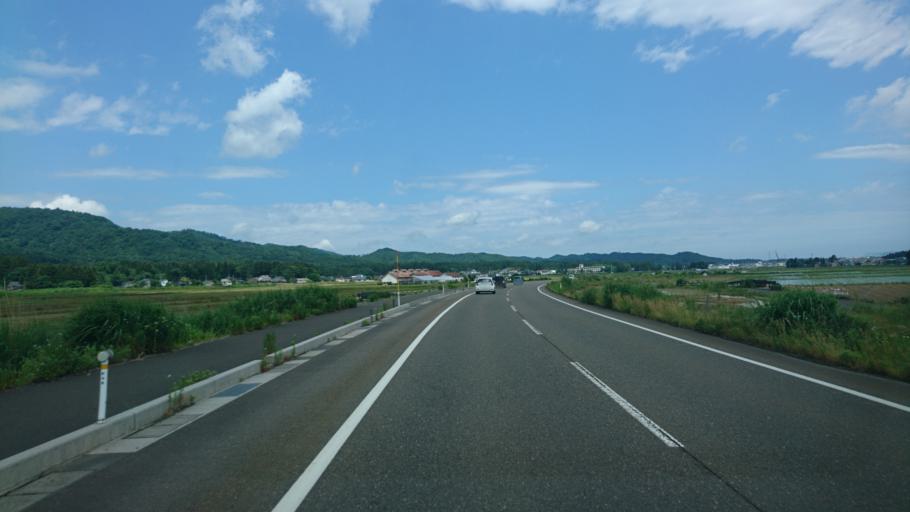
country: JP
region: Niigata
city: Arai
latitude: 37.0729
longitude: 138.2362
